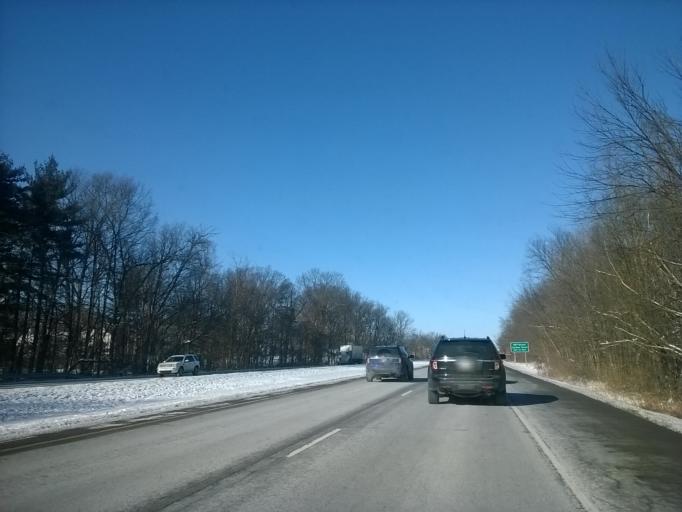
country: US
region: Indiana
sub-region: Hamilton County
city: Carmel
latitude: 39.9484
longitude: -86.1136
